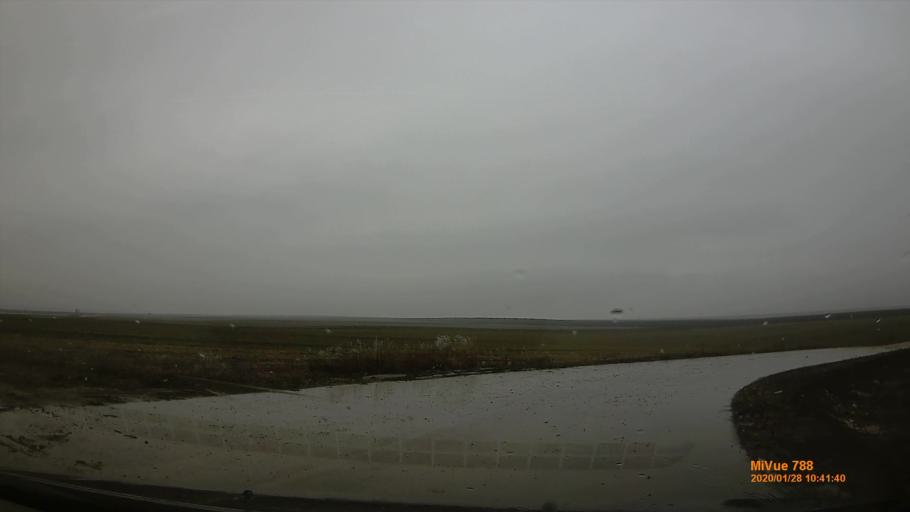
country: HU
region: Pest
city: Monor
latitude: 47.3604
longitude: 19.4867
